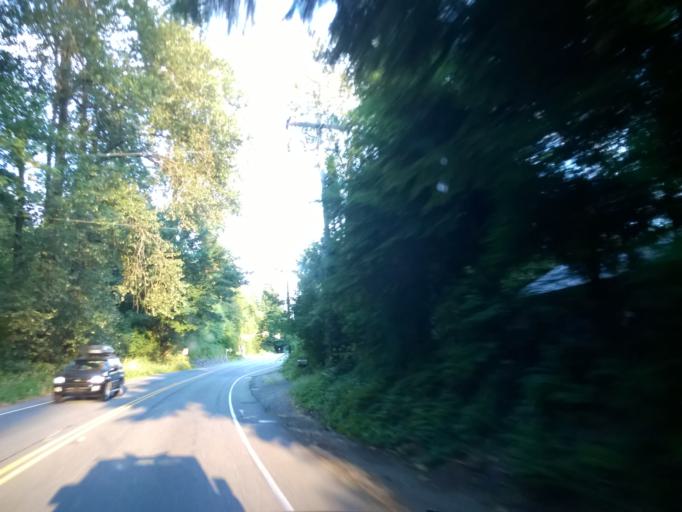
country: US
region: Washington
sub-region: King County
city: Cottage Lake
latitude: 47.7542
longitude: -122.0537
